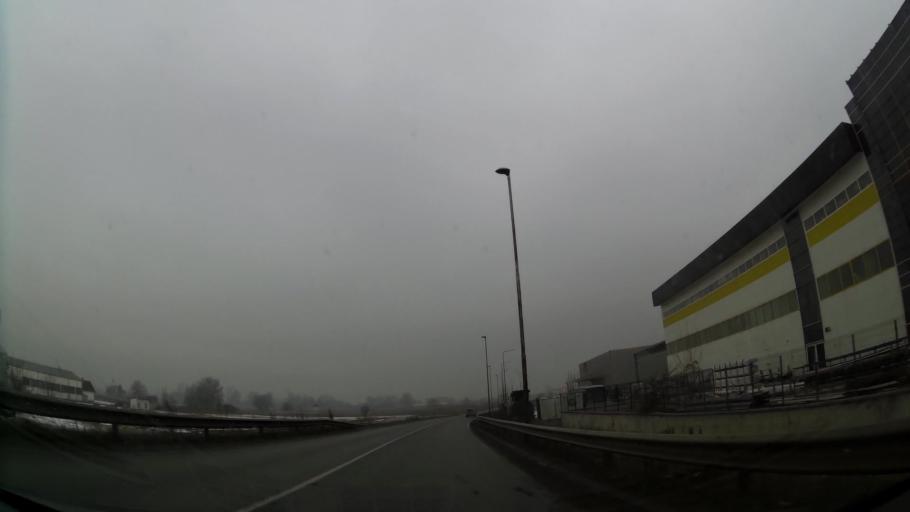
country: MK
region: Cucer-Sandevo
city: Chucher - Sandevo
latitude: 42.0557
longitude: 21.3786
